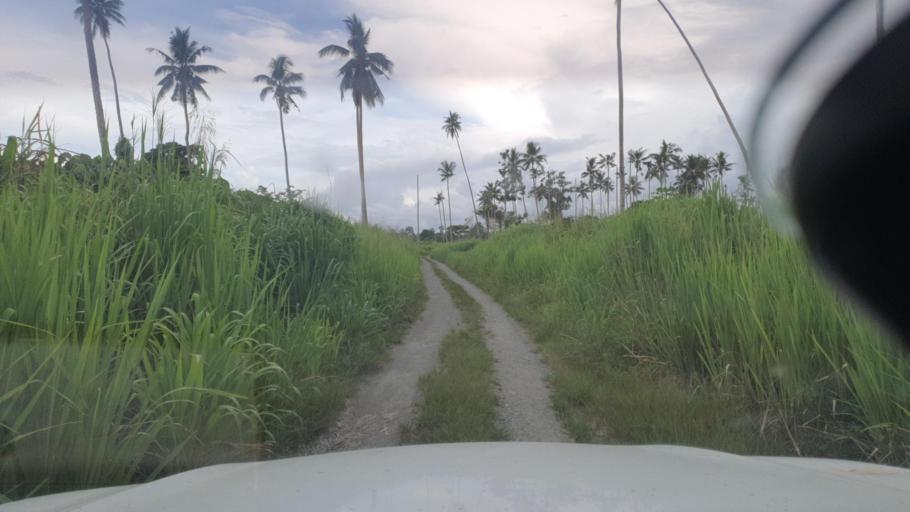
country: SB
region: Guadalcanal
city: Honiara
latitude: -9.4388
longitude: 160.2835
